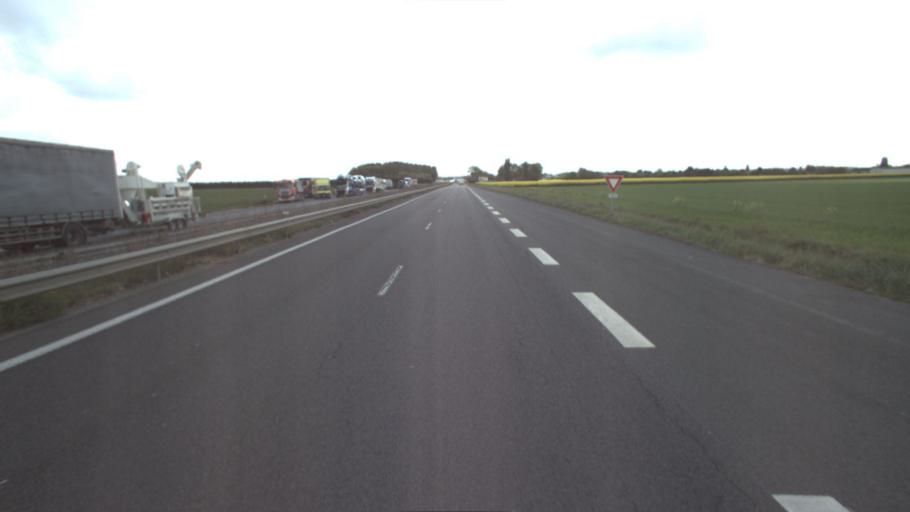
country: FR
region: Ile-de-France
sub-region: Departement de Seine-et-Marne
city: Rozay-en-Brie
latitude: 48.6918
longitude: 2.9160
